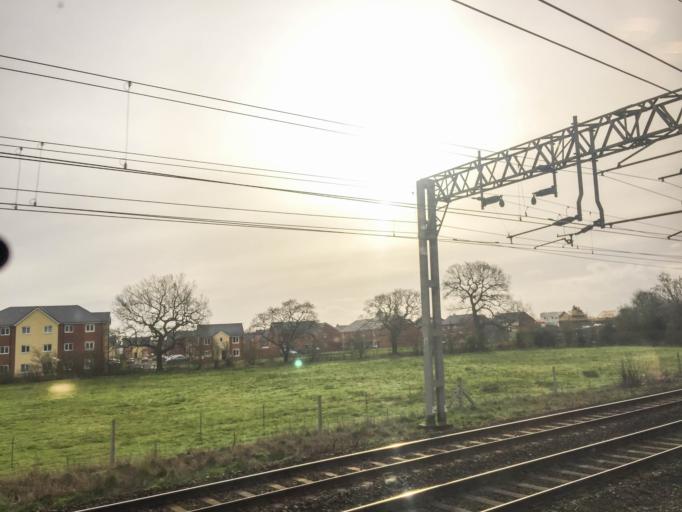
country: GB
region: England
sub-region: Cheshire East
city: Crewe
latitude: 53.1169
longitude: -2.4484
